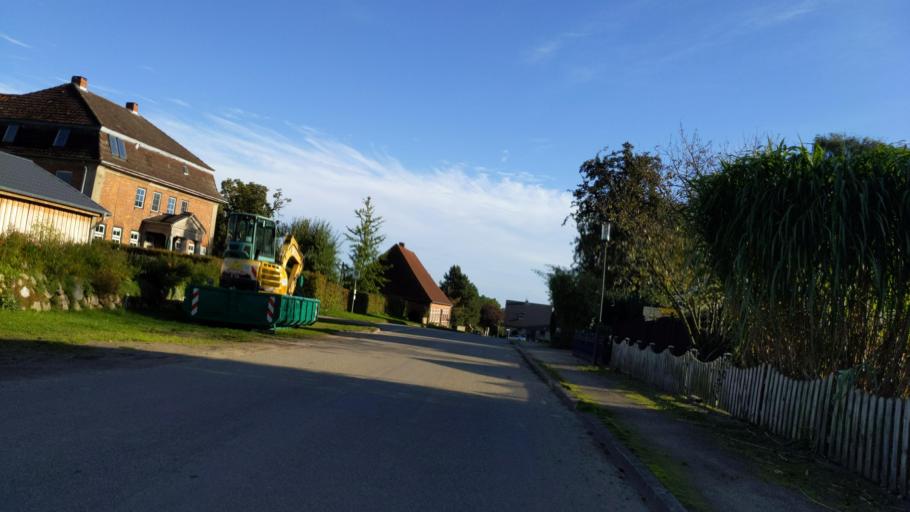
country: DE
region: Schleswig-Holstein
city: Ahrensbok
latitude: 54.0352
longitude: 10.6011
